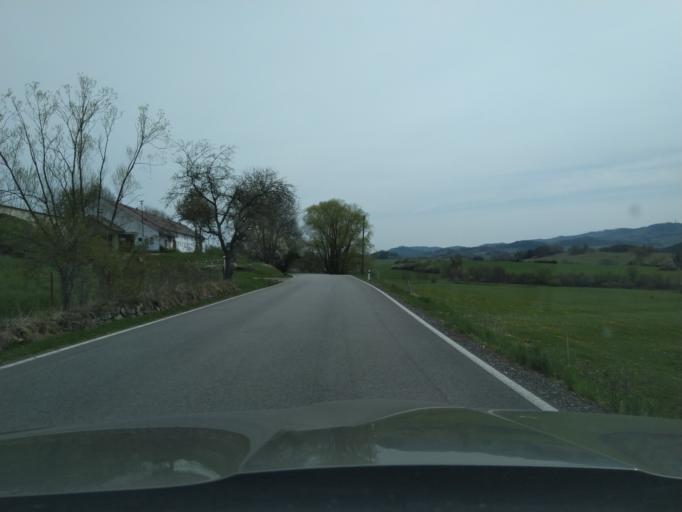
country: CZ
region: Jihocesky
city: Vacov
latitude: 49.1154
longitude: 13.7650
